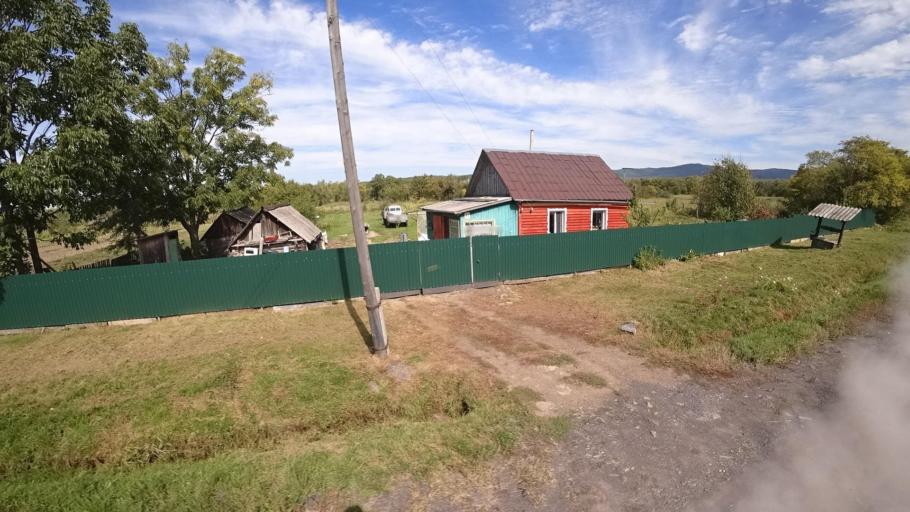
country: RU
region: Primorskiy
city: Yakovlevka
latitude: 44.4312
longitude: 133.5722
